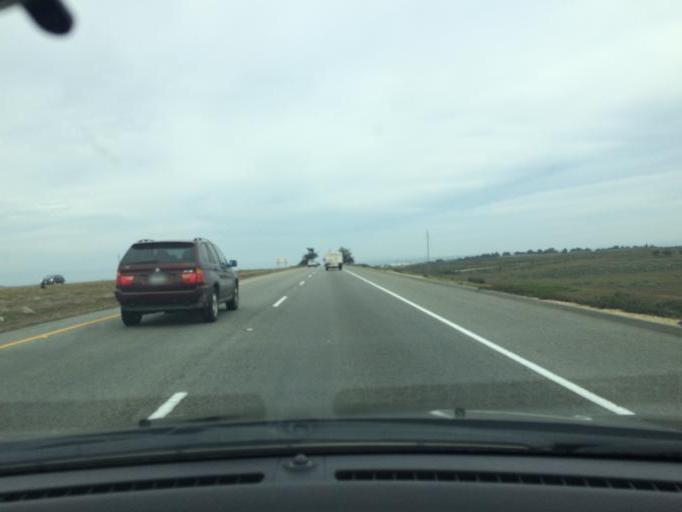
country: US
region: California
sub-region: Monterey County
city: Marina
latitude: 36.7092
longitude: -121.7976
